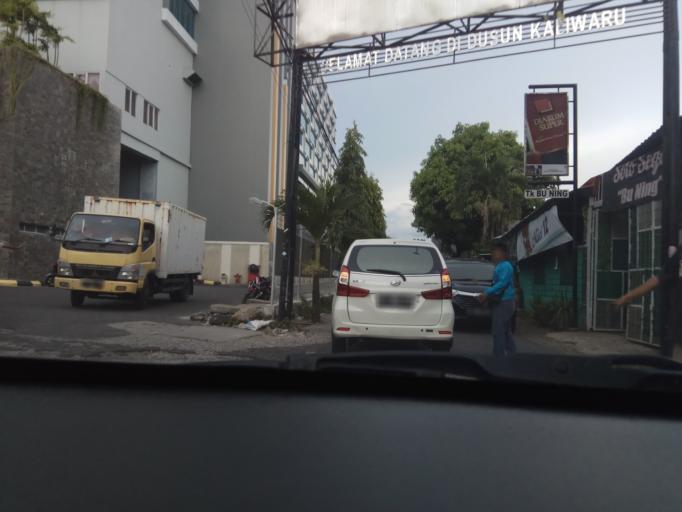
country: ID
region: Daerah Istimewa Yogyakarta
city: Depok
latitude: -7.7621
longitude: 110.3977
